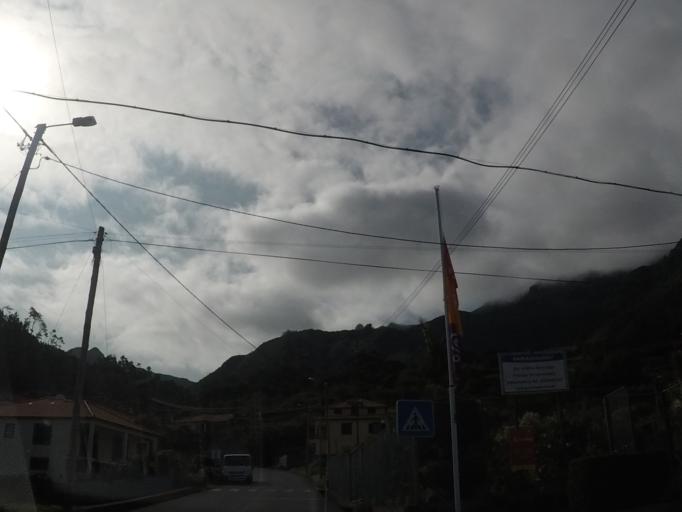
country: PT
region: Madeira
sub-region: Sao Vicente
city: Sao Vicente
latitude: 32.7818
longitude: -17.0437
